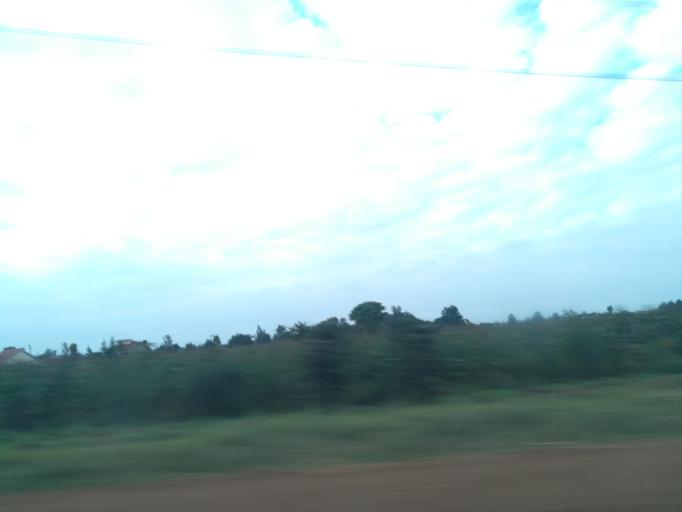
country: KE
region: Nairobi Area
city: Thika
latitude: -1.0376
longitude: 37.0615
